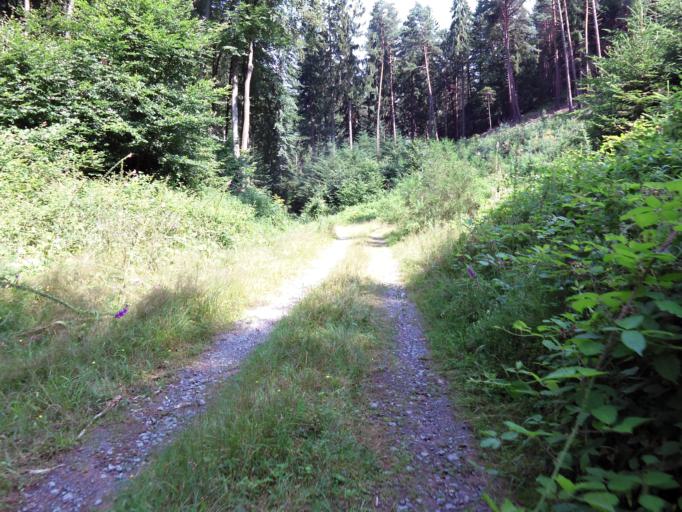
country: DE
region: Rheinland-Pfalz
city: Neidenfels
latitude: 49.4220
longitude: 8.0766
